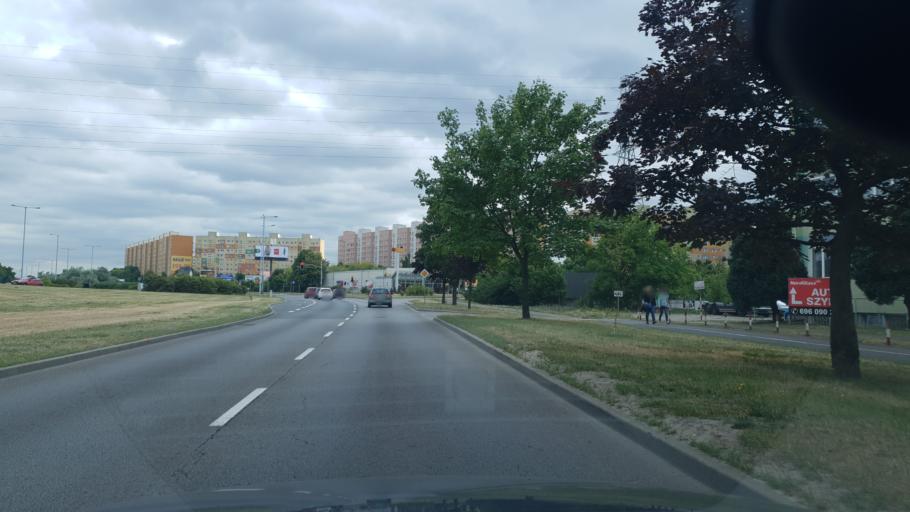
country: PL
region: Pomeranian Voivodeship
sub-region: Sopot
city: Sopot
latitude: 54.4005
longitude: 18.5924
